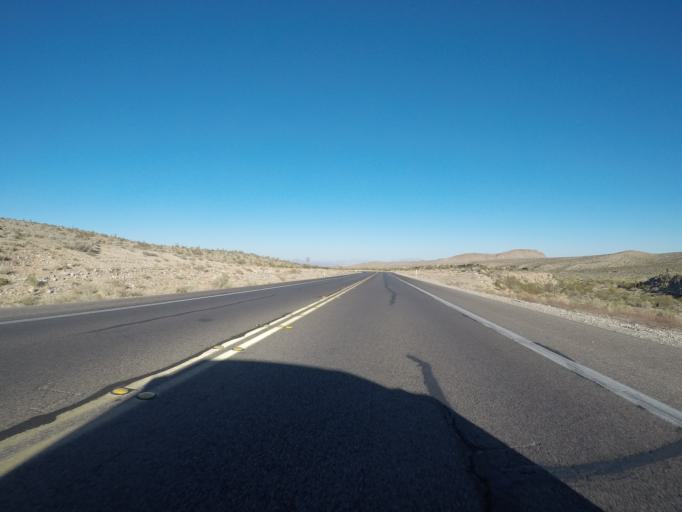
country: US
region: Nevada
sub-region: Clark County
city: Summerlin South
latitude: 36.1332
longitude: -115.4145
